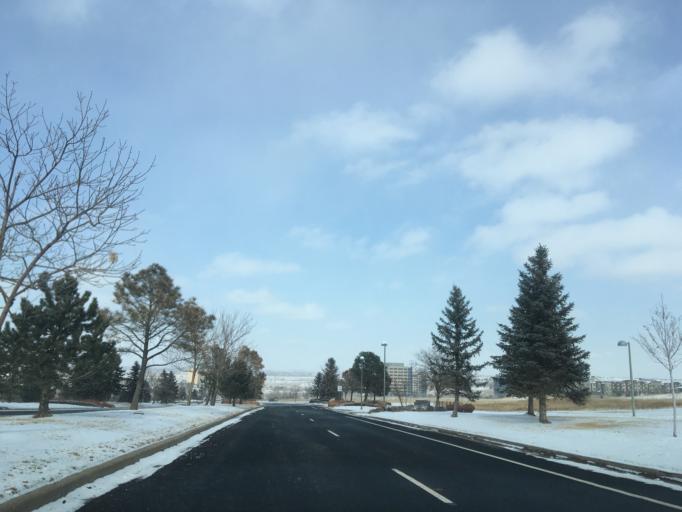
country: US
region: Colorado
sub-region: Broomfield County
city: Broomfield
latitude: 39.9174
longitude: -105.1231
